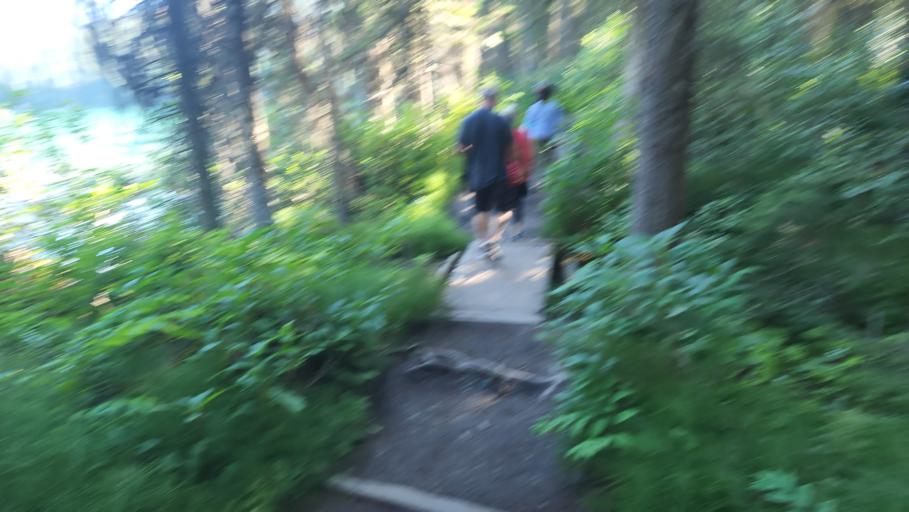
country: CA
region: Alberta
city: Lake Louise
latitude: 51.4371
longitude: -116.5287
